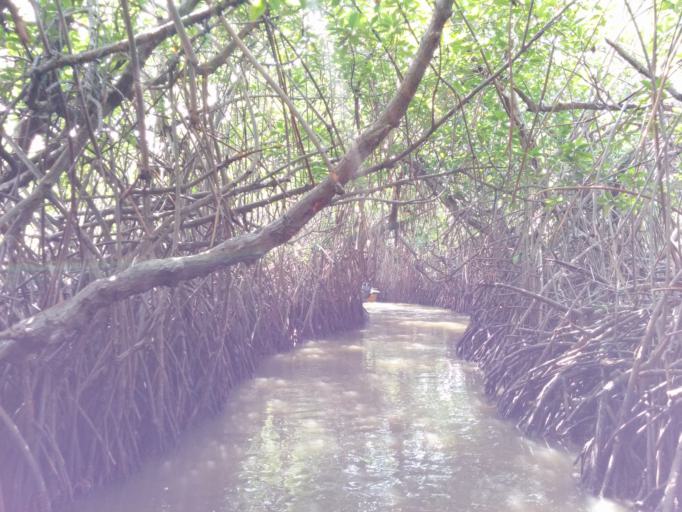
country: IN
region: Tamil Nadu
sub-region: Cuddalore
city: Annamalainagar
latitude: 11.4285
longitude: 79.7927
